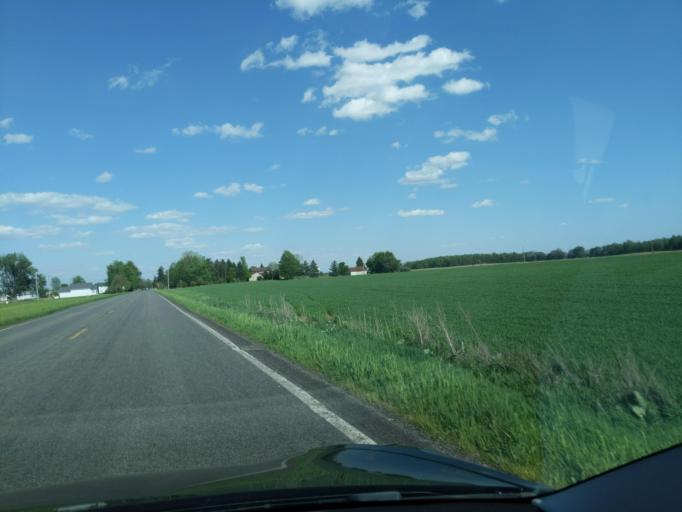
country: US
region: Michigan
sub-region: Ionia County
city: Lake Odessa
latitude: 42.7844
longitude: -85.1763
